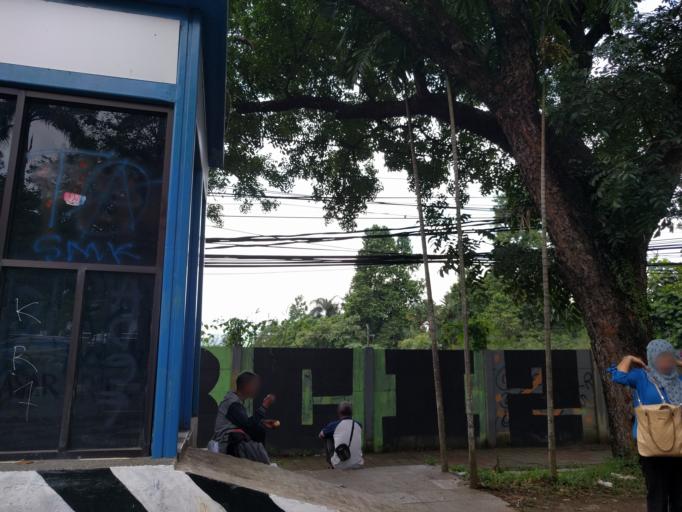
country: ID
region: West Java
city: Bogor
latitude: -6.5803
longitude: 106.8070
